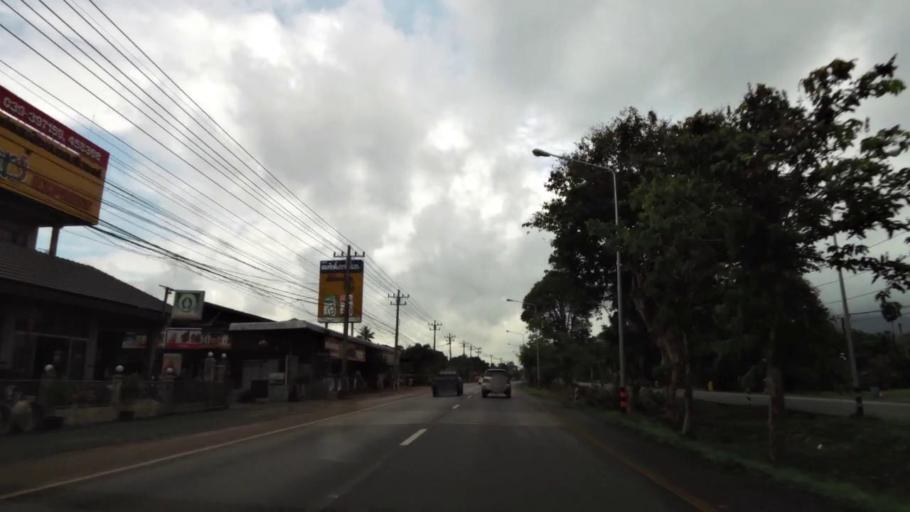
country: TH
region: Chanthaburi
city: Khlung
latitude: 12.5019
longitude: 102.1705
